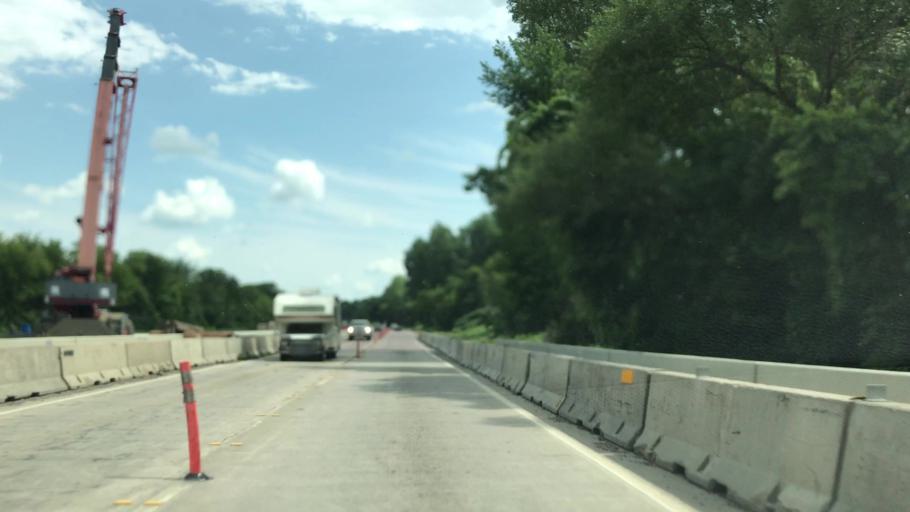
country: US
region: Minnesota
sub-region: Nicollet County
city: Saint Peter
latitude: 44.3658
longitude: -93.9638
